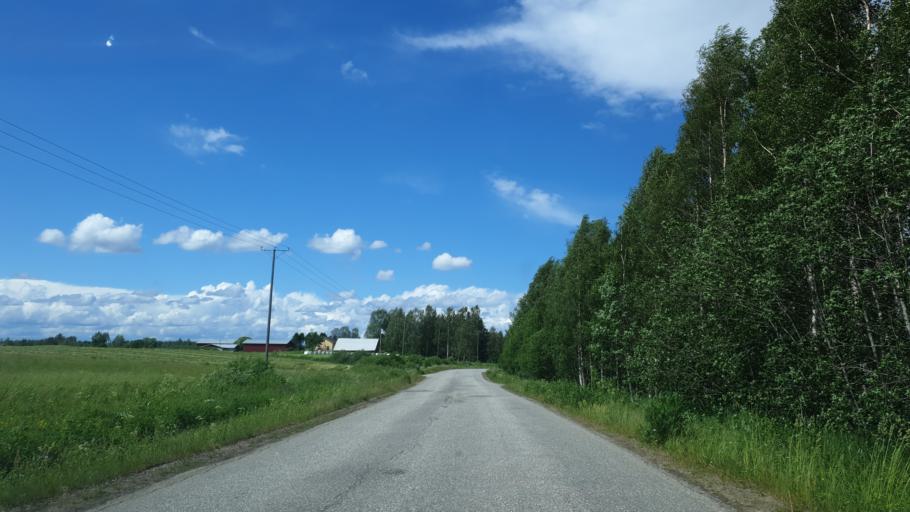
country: FI
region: Northern Savo
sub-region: Koillis-Savo
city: Kaavi
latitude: 62.9933
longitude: 28.7218
